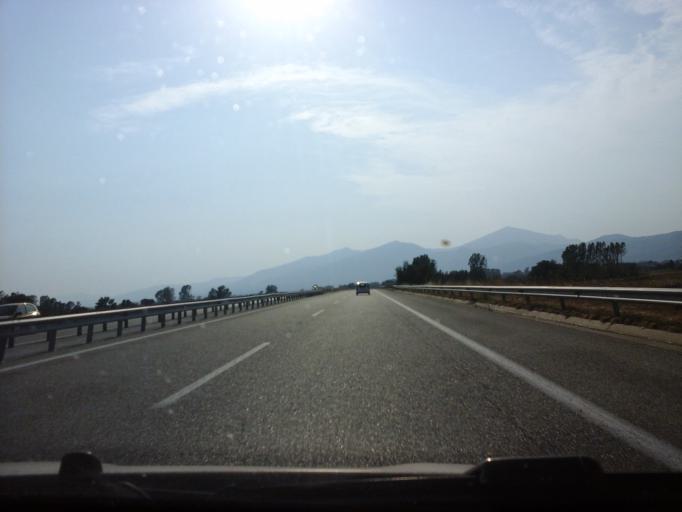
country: GR
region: East Macedonia and Thrace
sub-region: Nomos Xanthis
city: Selero
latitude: 41.1179
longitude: 25.0009
